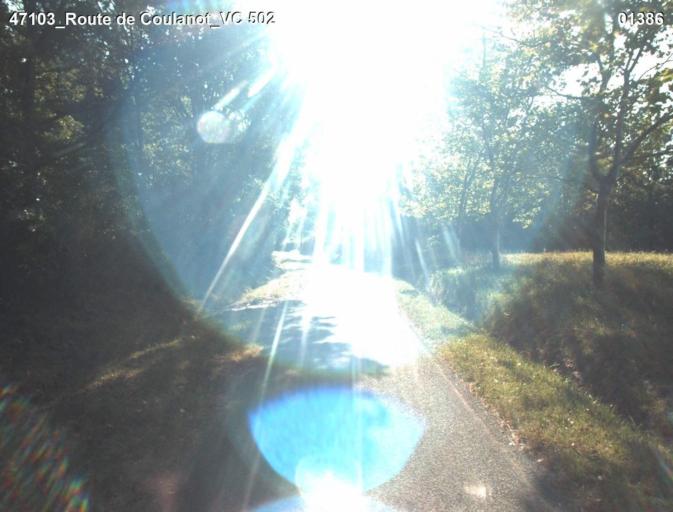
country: FR
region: Aquitaine
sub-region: Departement du Lot-et-Garonne
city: Nerac
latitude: 44.0708
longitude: 0.3444
